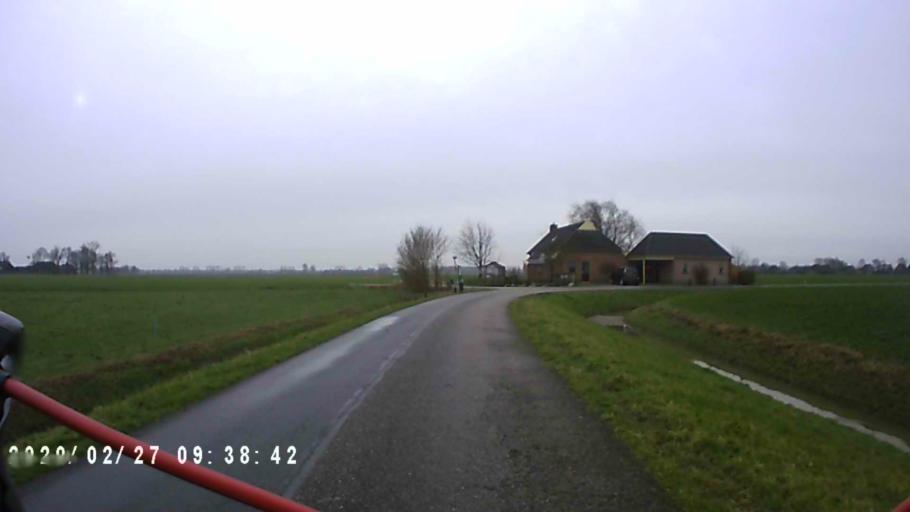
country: NL
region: Groningen
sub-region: Gemeente Zuidhorn
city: Aduard
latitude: 53.2788
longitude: 6.4303
